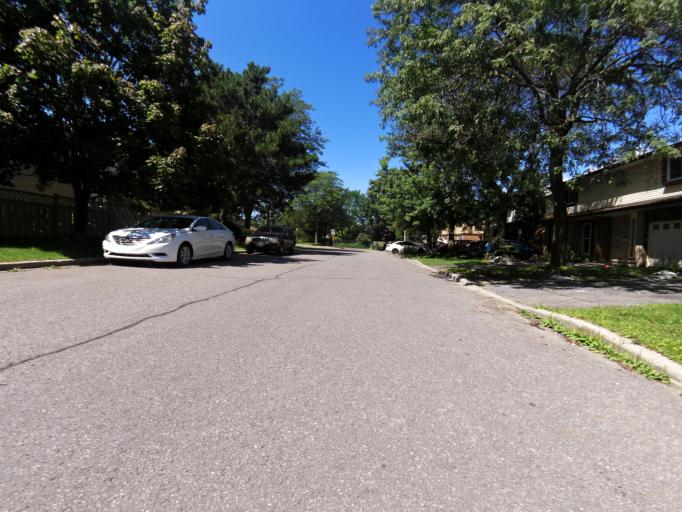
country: CA
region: Ontario
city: Ottawa
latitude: 45.3447
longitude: -75.6692
